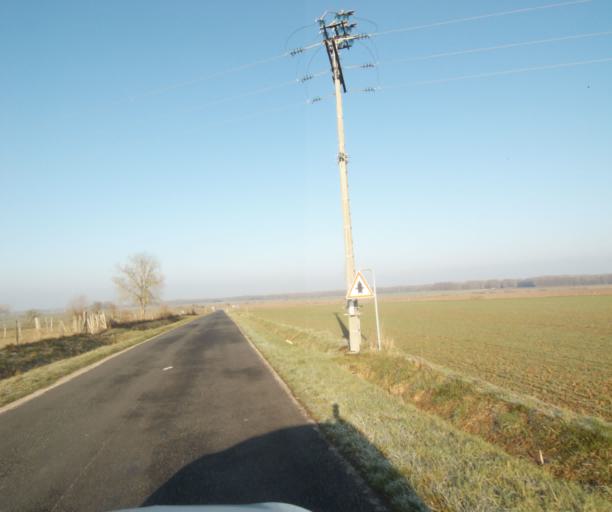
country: FR
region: Champagne-Ardenne
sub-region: Departement de la Haute-Marne
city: Montier-en-Der
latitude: 48.5046
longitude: 4.7350
